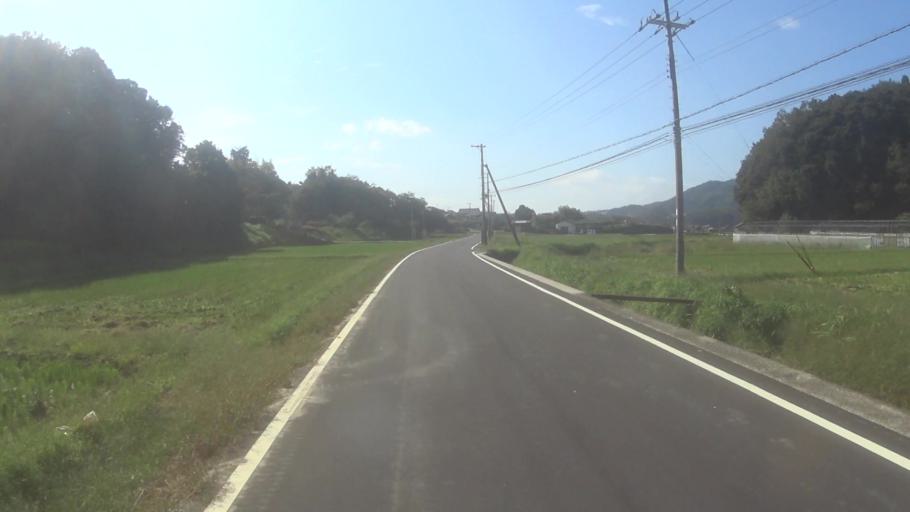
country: JP
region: Kyoto
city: Miyazu
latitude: 35.6805
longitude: 135.1065
